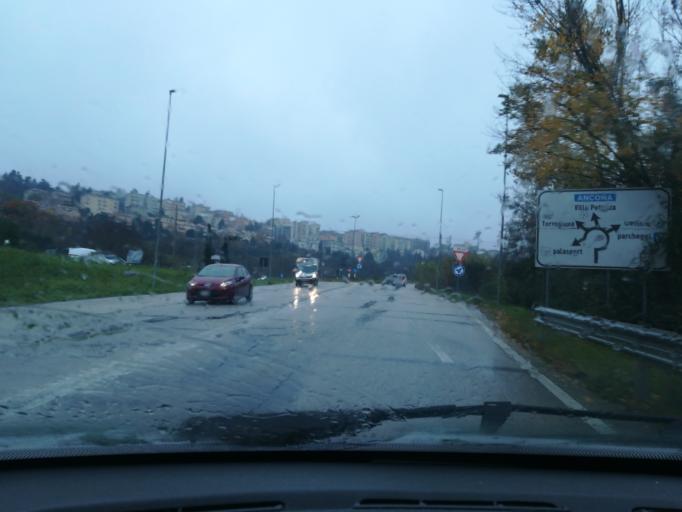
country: IT
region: The Marches
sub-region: Provincia di Macerata
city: Macerata
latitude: 43.2945
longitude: 13.4426
